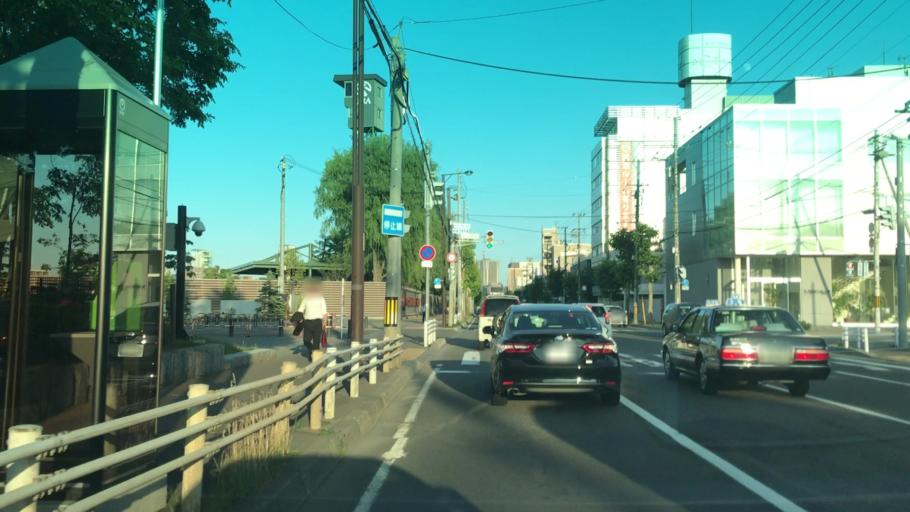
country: JP
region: Hokkaido
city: Sapporo
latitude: 43.0752
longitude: 141.3237
